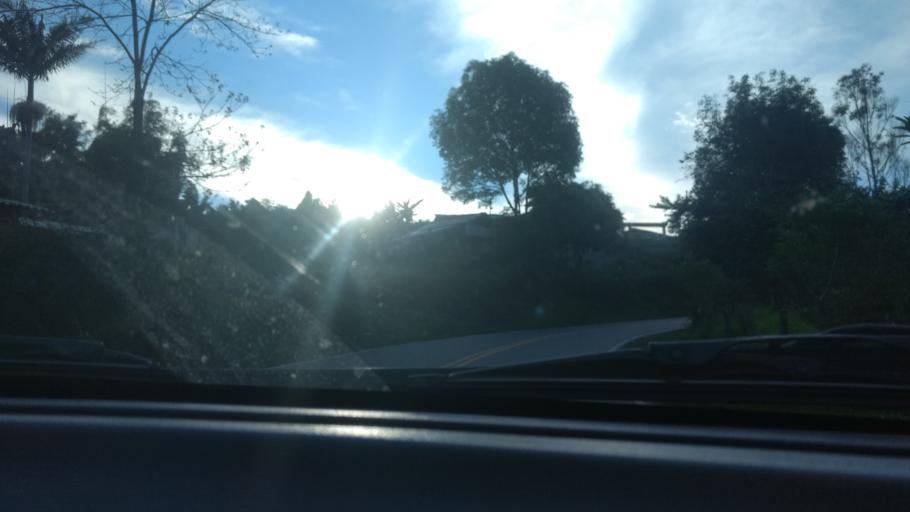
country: CO
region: Cauca
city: Rosas
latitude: 2.3184
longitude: -76.6883
